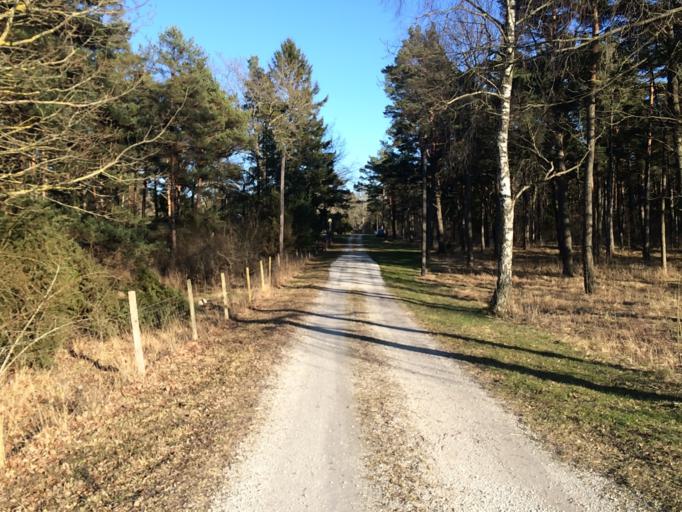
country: SE
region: Gotland
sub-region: Gotland
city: Slite
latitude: 57.5851
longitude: 18.6086
